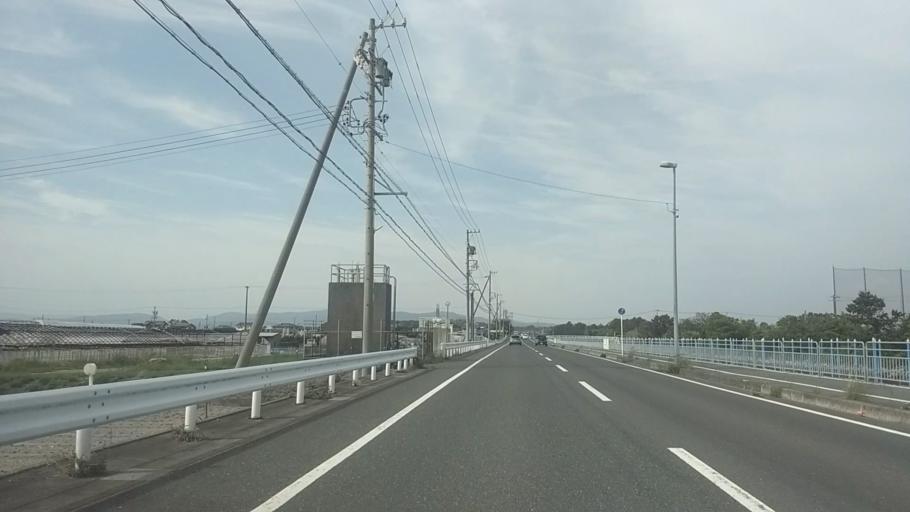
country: JP
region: Shizuoka
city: Kosai-shi
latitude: 34.7138
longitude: 137.5906
